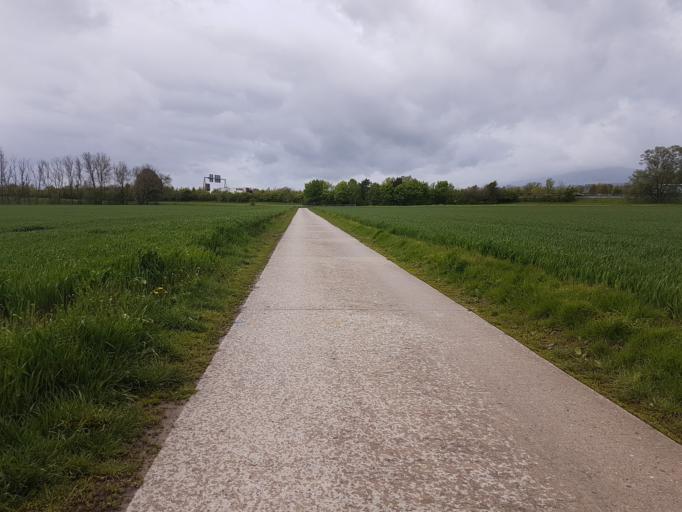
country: CH
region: Vaud
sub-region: Jura-Nord vaudois District
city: Chavornay
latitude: 46.7237
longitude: 6.5732
